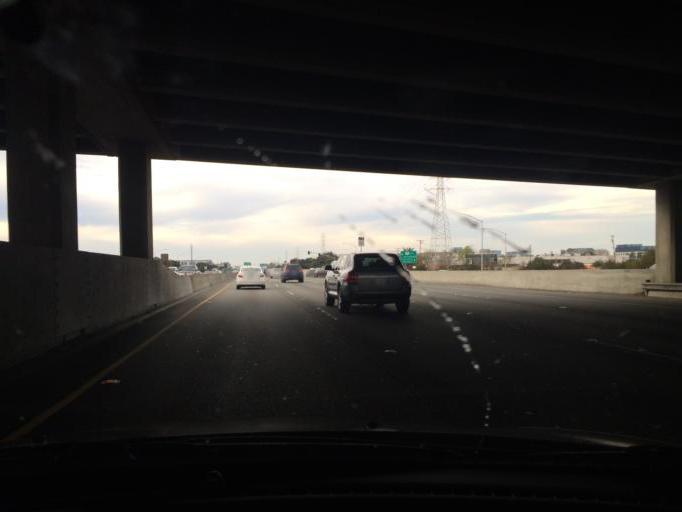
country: US
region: California
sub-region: San Mateo County
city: San Carlos
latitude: 37.5139
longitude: -122.2560
